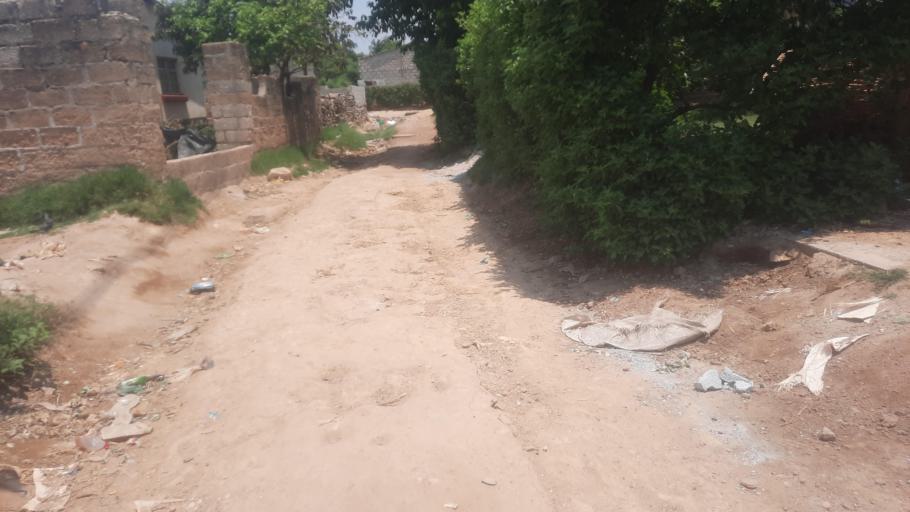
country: ZM
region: Lusaka
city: Lusaka
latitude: -15.4015
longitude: 28.3736
